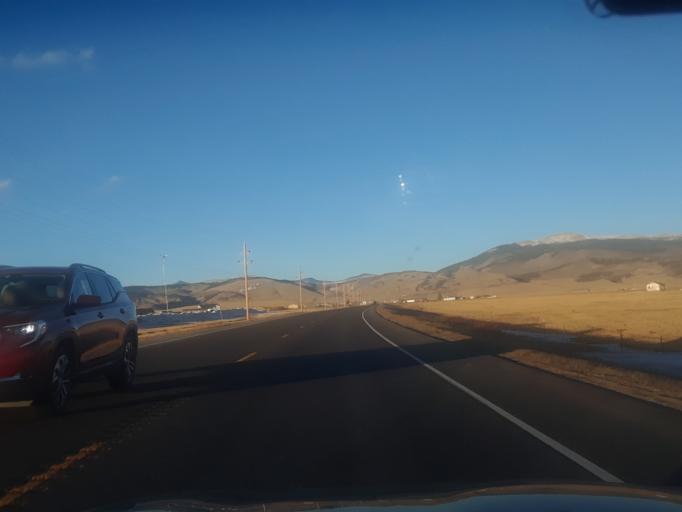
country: US
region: Colorado
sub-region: Park County
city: Fairplay
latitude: 39.3655
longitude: -105.8130
